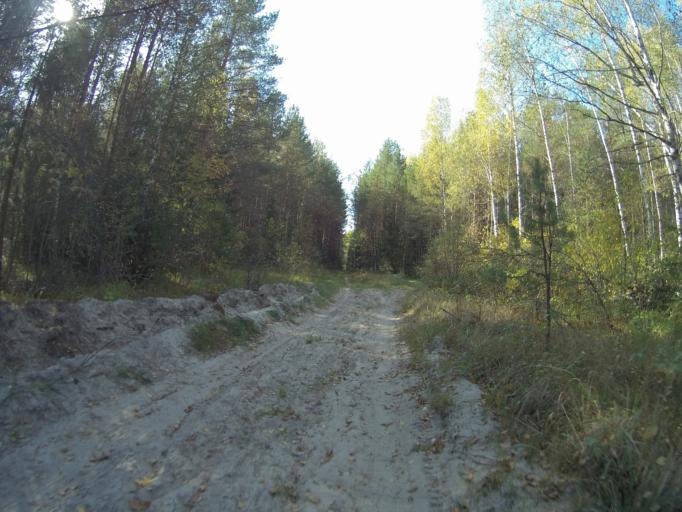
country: RU
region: Vladimir
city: Vorsha
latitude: 55.9677
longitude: 40.1283
